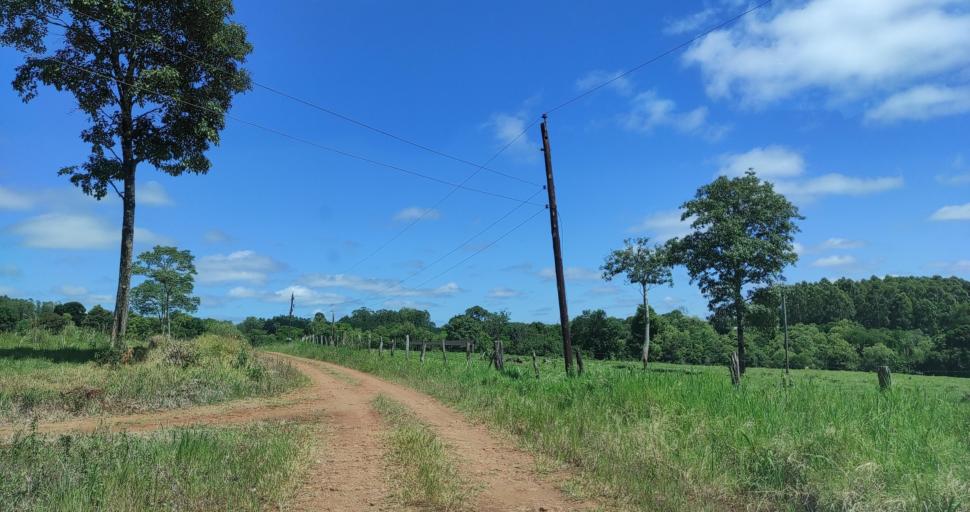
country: AR
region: Misiones
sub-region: Departamento de Veinticinco de Mayo
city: Veinticinco de Mayo
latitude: -27.4155
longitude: -54.7236
